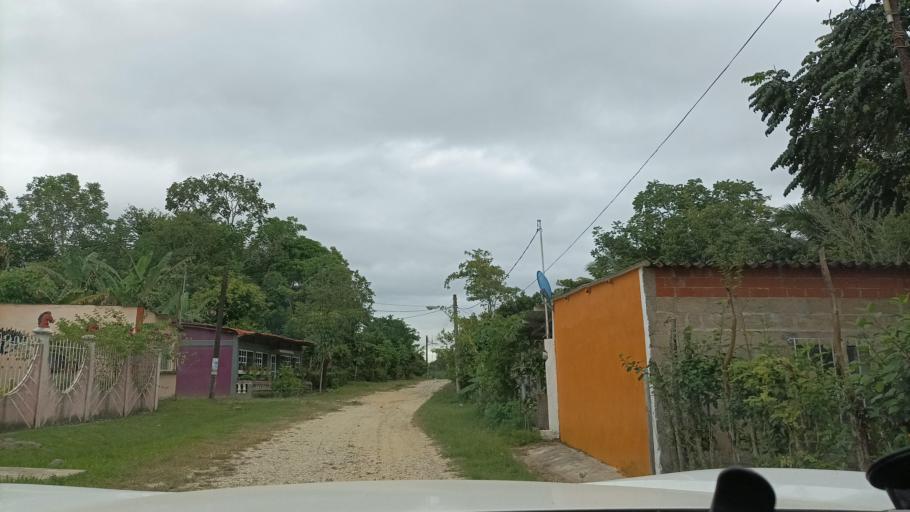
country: MX
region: Veracruz
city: Hidalgotitlan
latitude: 17.8062
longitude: -94.5416
